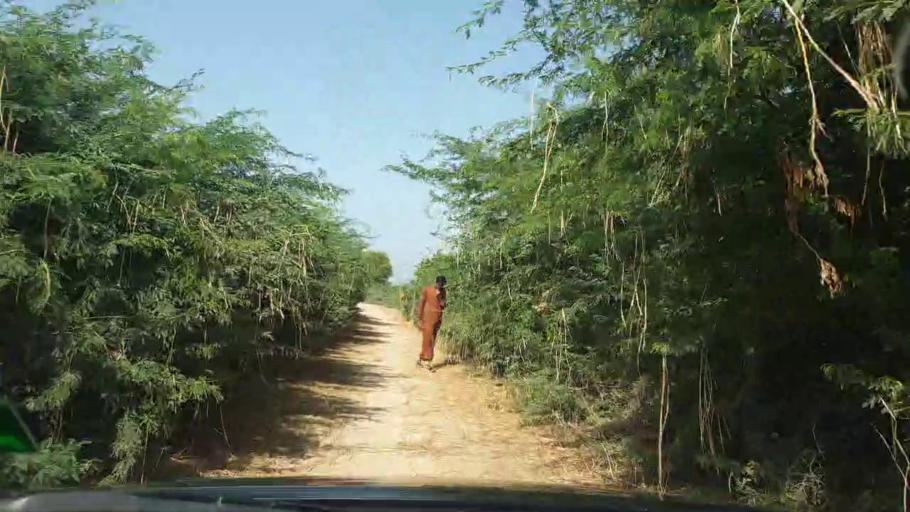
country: PK
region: Sindh
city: Tando Bago
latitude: 24.7732
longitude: 68.9472
